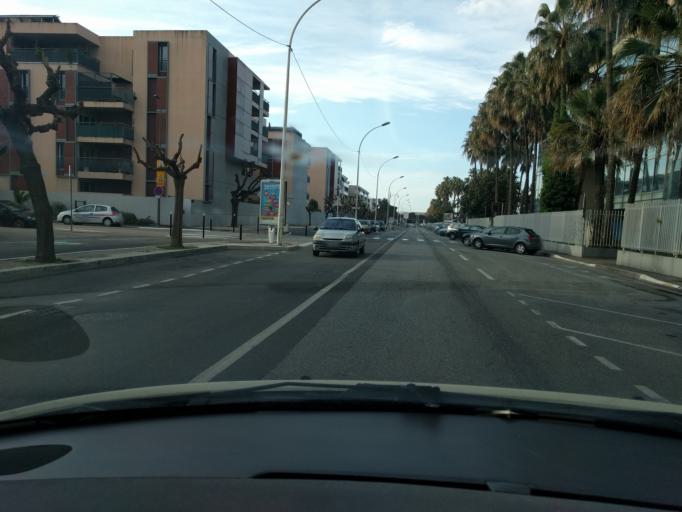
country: FR
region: Provence-Alpes-Cote d'Azur
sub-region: Departement des Alpes-Maritimes
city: Mandelieu-la-Napoule
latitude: 43.5533
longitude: 6.9659
